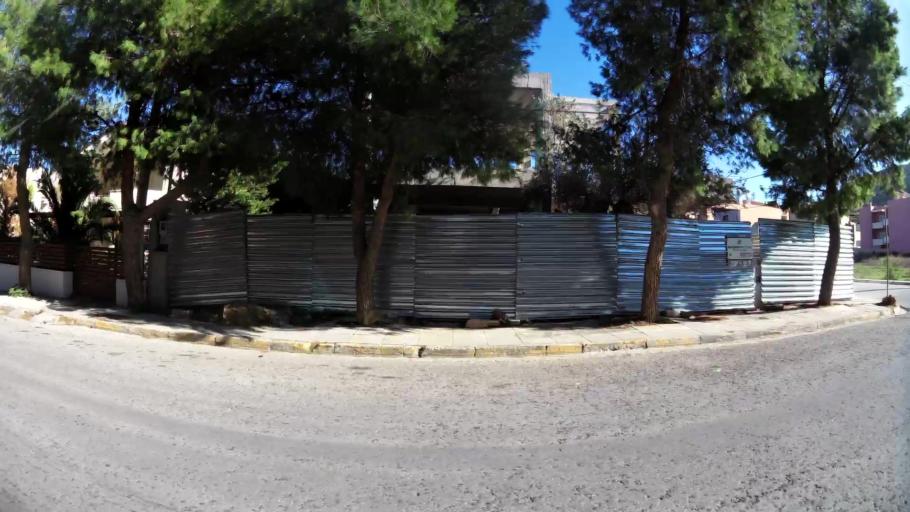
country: GR
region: Attica
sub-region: Nomarchia Anatolikis Attikis
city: Kalyvia Thorikou
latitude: 37.8337
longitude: 23.9299
